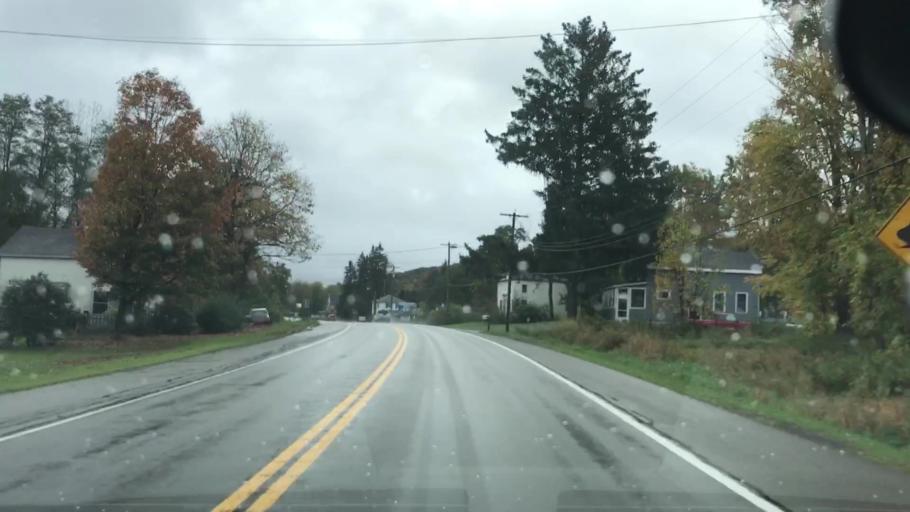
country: US
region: New York
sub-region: Erie County
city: Springville
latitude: 42.4046
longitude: -78.6870
